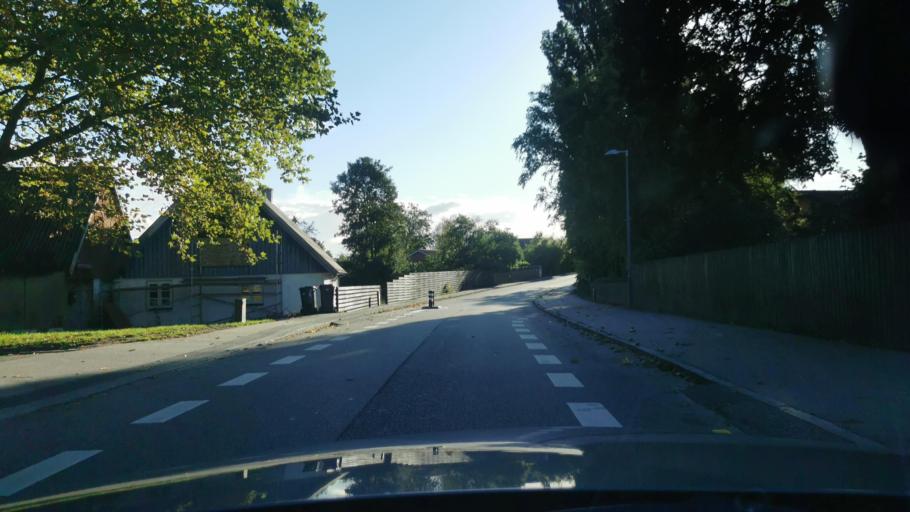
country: DK
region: Zealand
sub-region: Kalundborg Kommune
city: Svebolle
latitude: 55.6532
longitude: 11.2807
